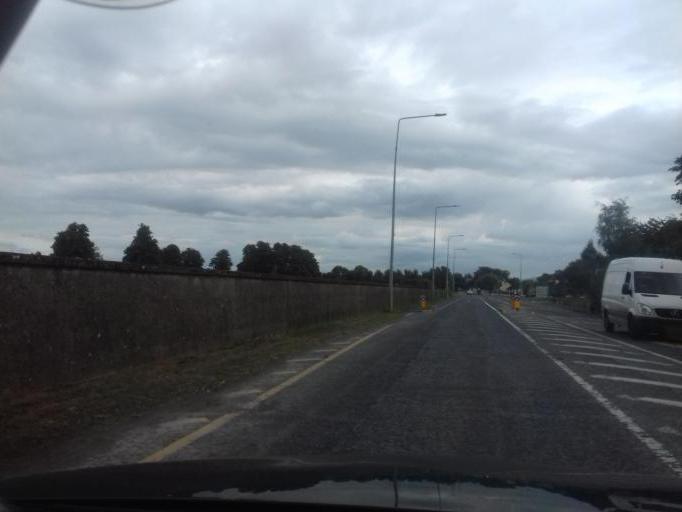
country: IE
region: Leinster
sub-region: County Carlow
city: Bagenalstown
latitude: 52.6824
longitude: -7.0229
